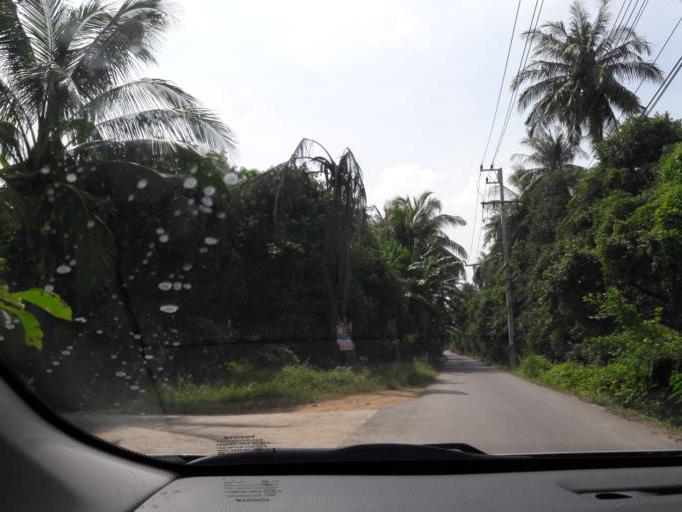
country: TH
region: Ang Thong
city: Ang Thong
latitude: 14.5734
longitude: 100.4402
